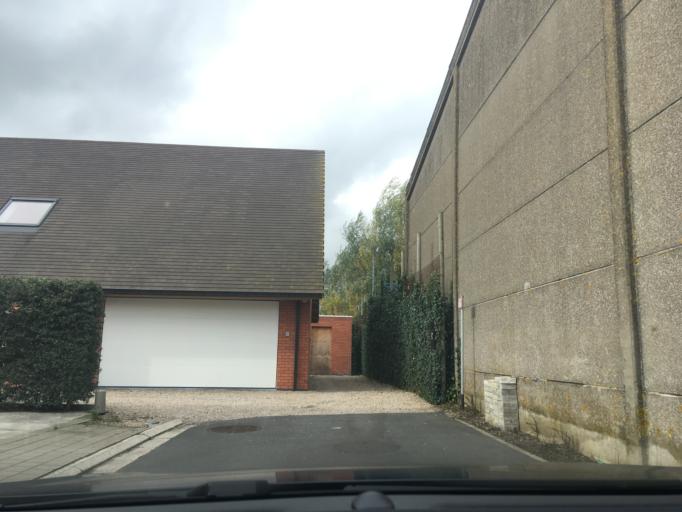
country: BE
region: Flanders
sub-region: Provincie West-Vlaanderen
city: Moorslede
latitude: 50.8914
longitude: 3.0510
